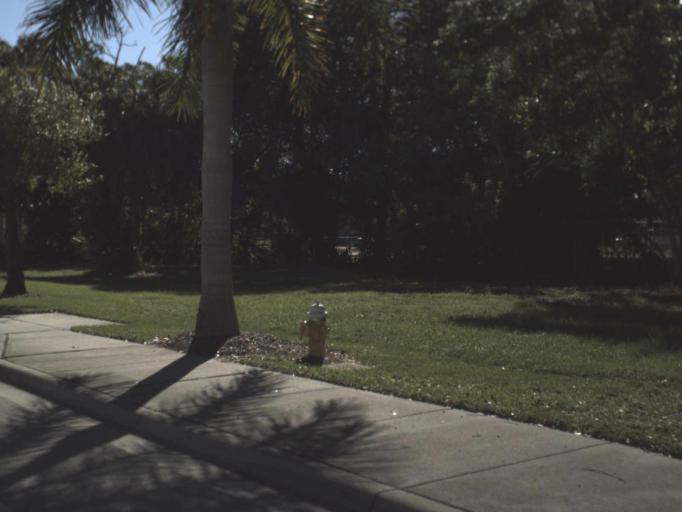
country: US
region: Florida
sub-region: Lee County
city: Fort Myers
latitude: 26.6408
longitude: -81.8539
